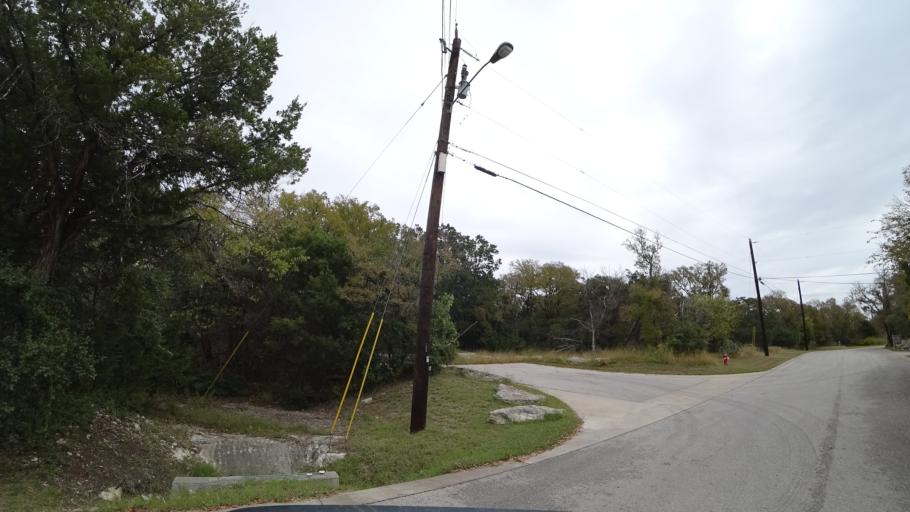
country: US
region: Texas
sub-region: Williamson County
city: Round Rock
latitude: 30.5145
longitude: -97.6988
